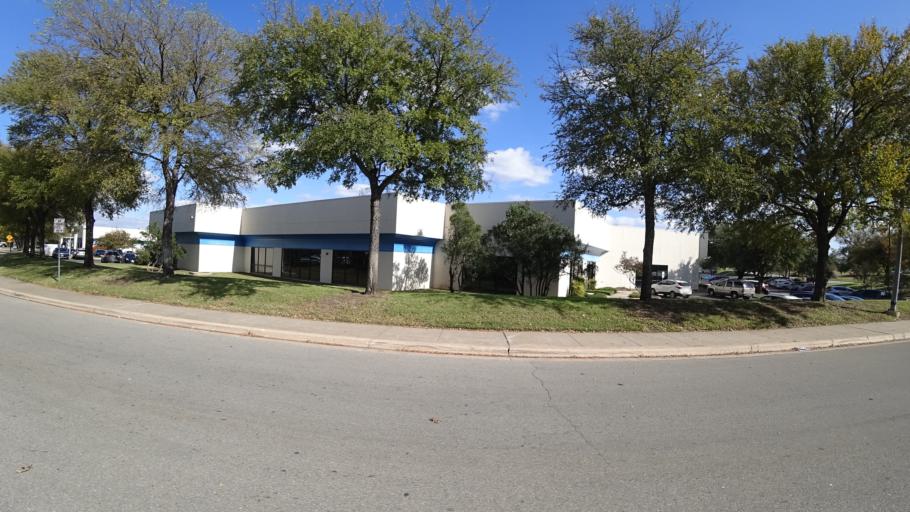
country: US
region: Texas
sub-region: Travis County
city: Wells Branch
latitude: 30.4740
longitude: -97.6782
